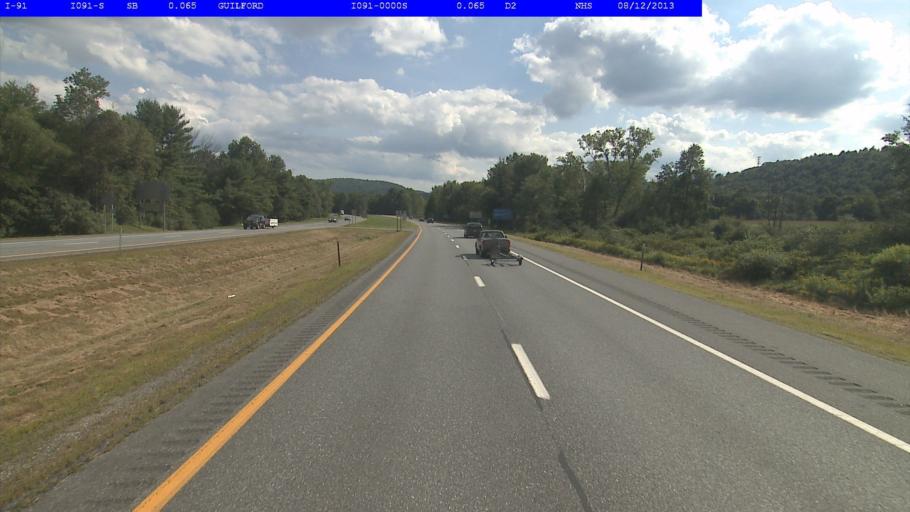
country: US
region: Massachusetts
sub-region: Franklin County
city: Bernardston
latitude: 42.7310
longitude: -72.5701
